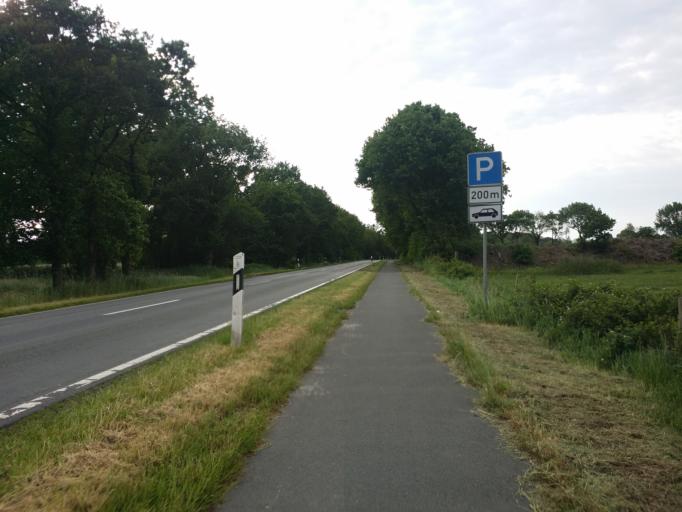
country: DE
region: Lower Saxony
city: Friedeburg
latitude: 53.5105
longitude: 7.7994
